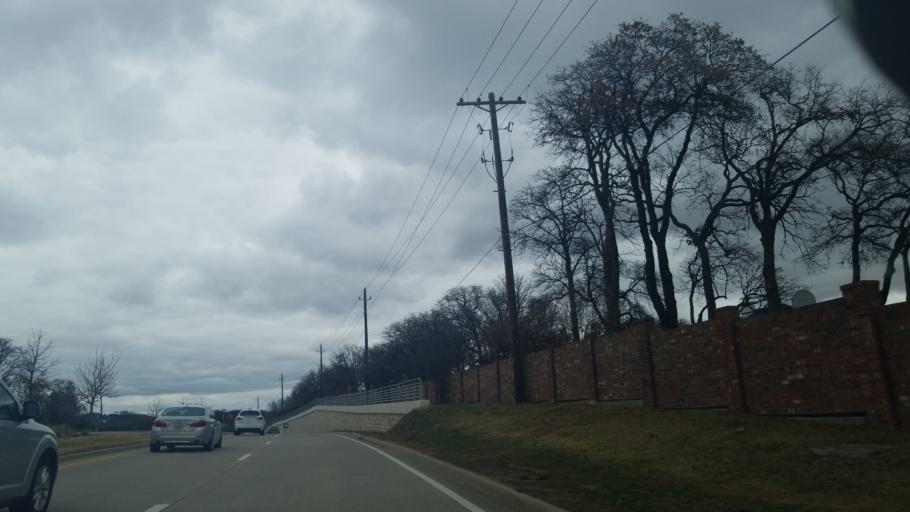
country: US
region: Texas
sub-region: Denton County
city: Copper Canyon
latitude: 33.0893
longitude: -97.0783
